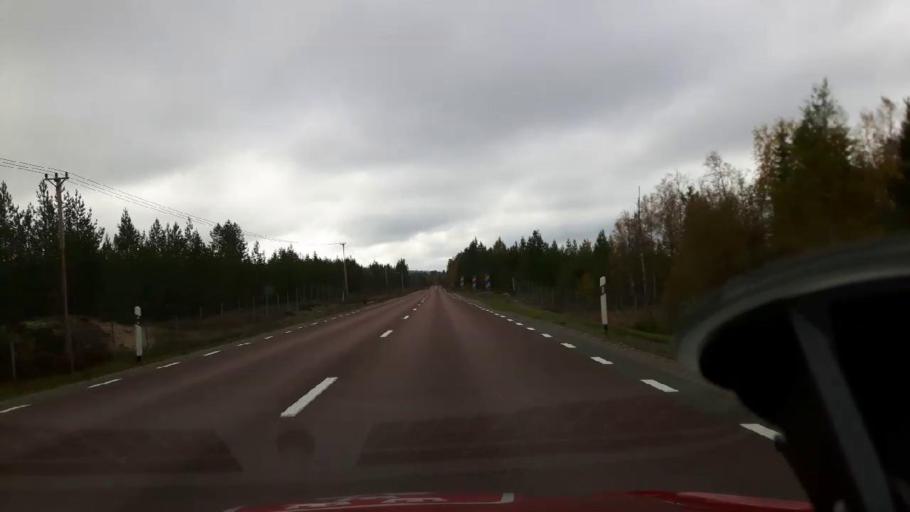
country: SE
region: Jaemtland
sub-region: Harjedalens Kommun
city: Sveg
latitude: 62.2291
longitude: 14.8430
